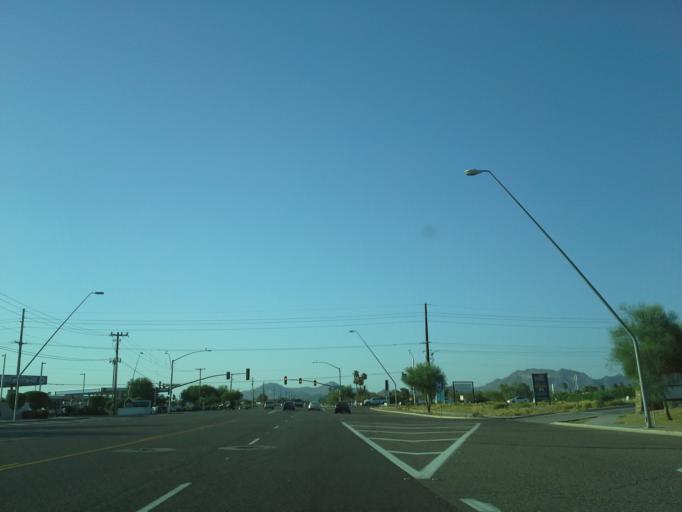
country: US
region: Arizona
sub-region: Pinal County
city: Apache Junction
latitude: 33.3919
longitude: -111.6327
